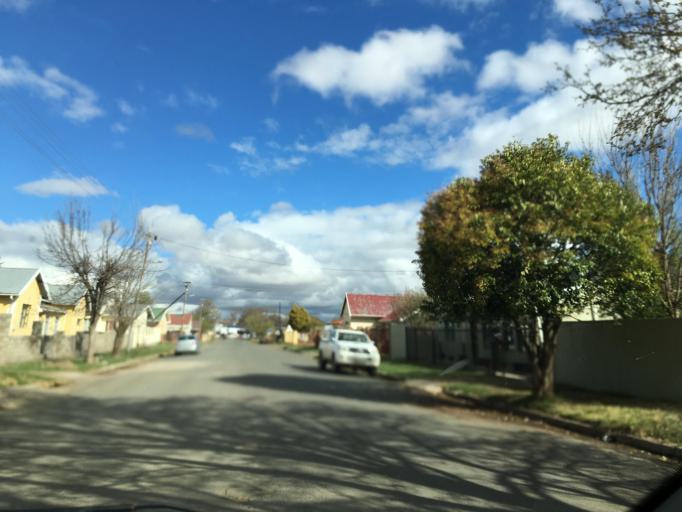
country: ZA
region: Eastern Cape
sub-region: Chris Hani District Municipality
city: Elliot
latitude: -31.3302
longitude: 27.8524
